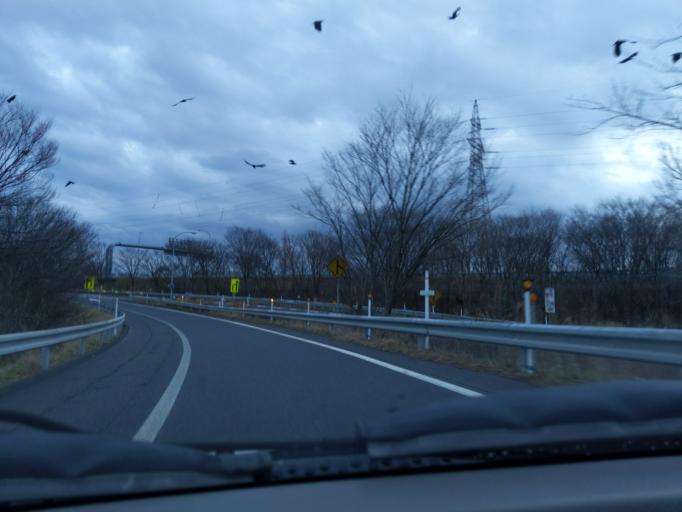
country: JP
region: Niigata
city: Niigata-shi
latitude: 37.8711
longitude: 139.0427
